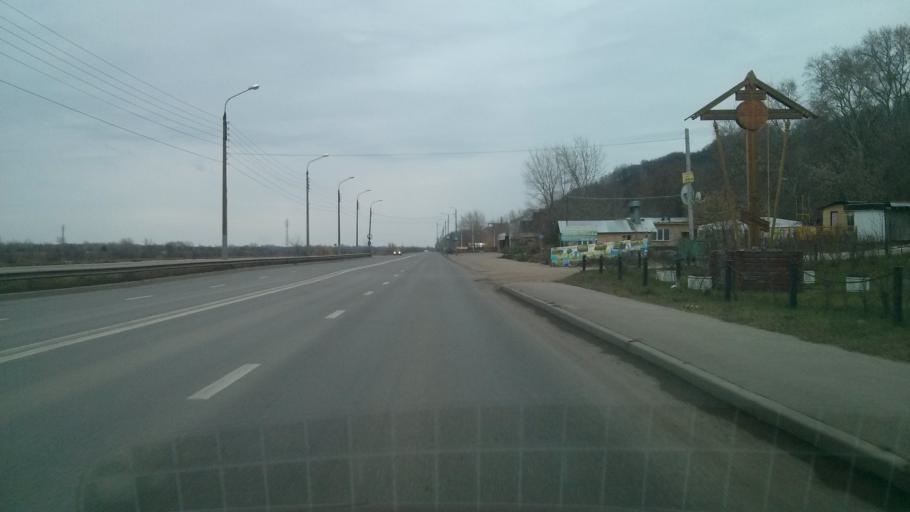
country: RU
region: Nizjnij Novgorod
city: Bor
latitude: 56.3242
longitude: 44.0543
